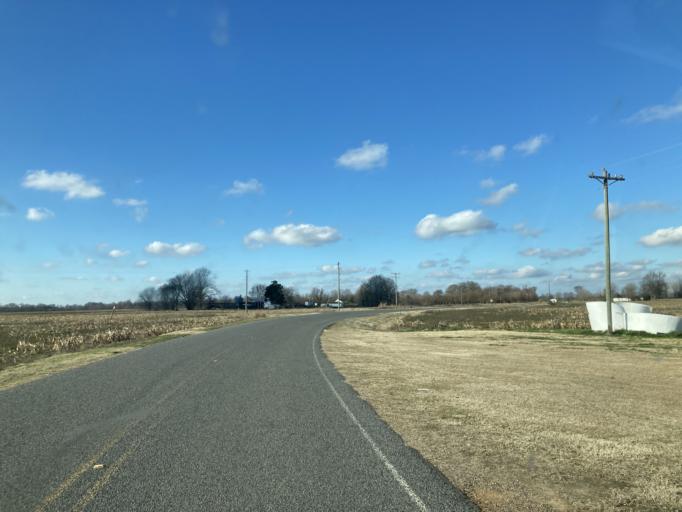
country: US
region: Mississippi
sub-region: Yazoo County
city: Yazoo City
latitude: 32.9270
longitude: -90.4708
